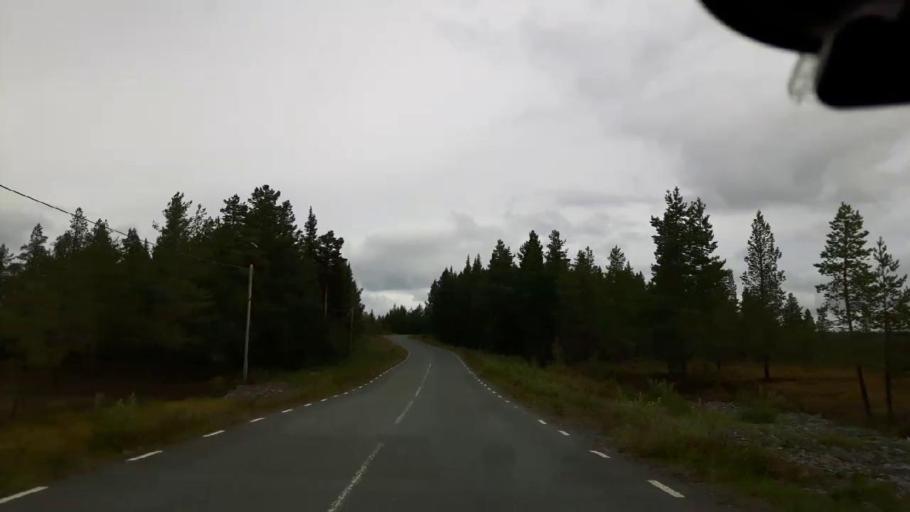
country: SE
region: Jaemtland
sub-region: Krokoms Kommun
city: Valla
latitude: 63.6659
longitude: 13.8588
